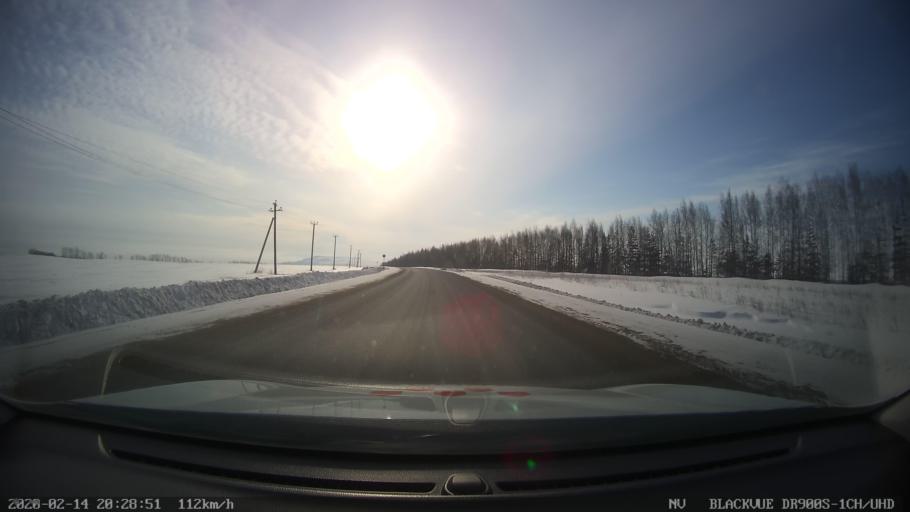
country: RU
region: Tatarstan
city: Stolbishchi
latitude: 55.4569
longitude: 48.9777
